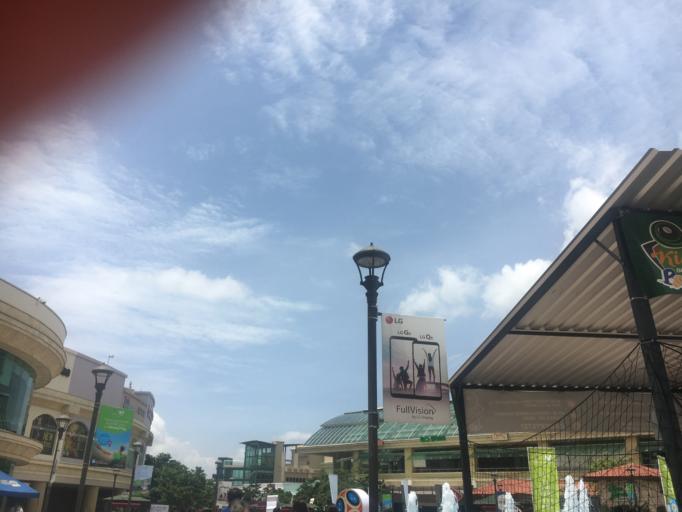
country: SV
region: La Libertad
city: Antiguo Cuscatlan
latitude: 13.6771
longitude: -89.2547
